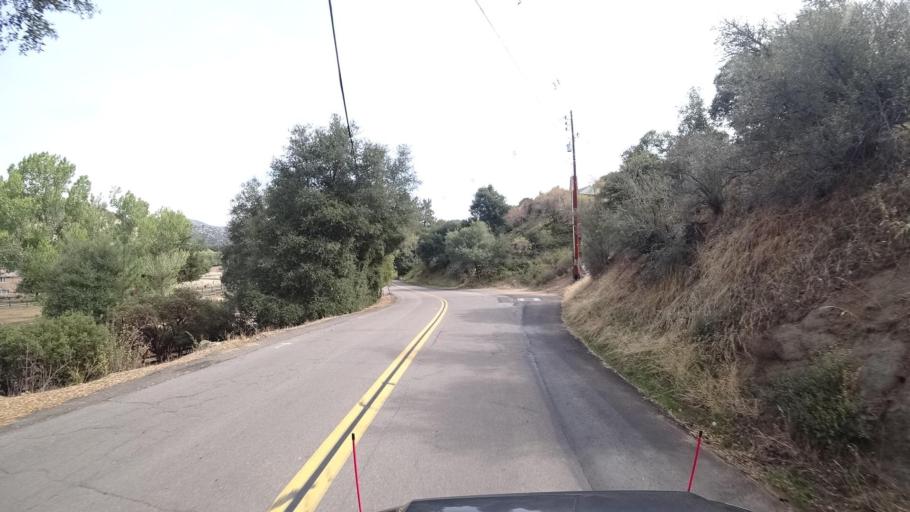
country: US
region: California
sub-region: San Diego County
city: Descanso
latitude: 32.8640
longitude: -116.6259
